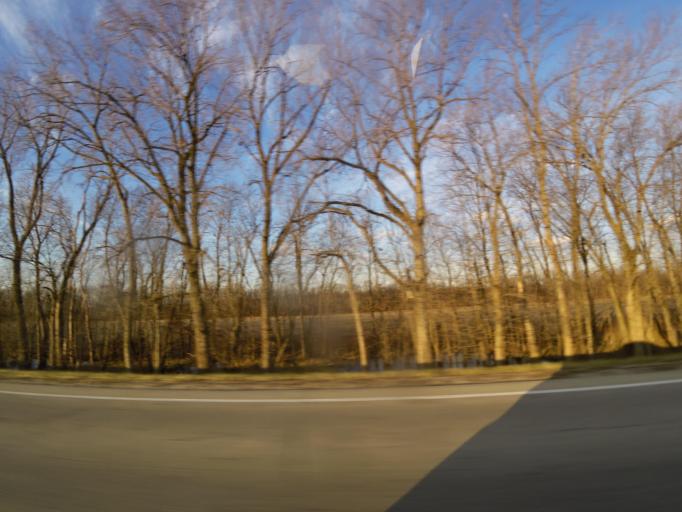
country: US
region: Illinois
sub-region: Fayette County
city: Vandalia
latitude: 38.9494
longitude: -89.0851
